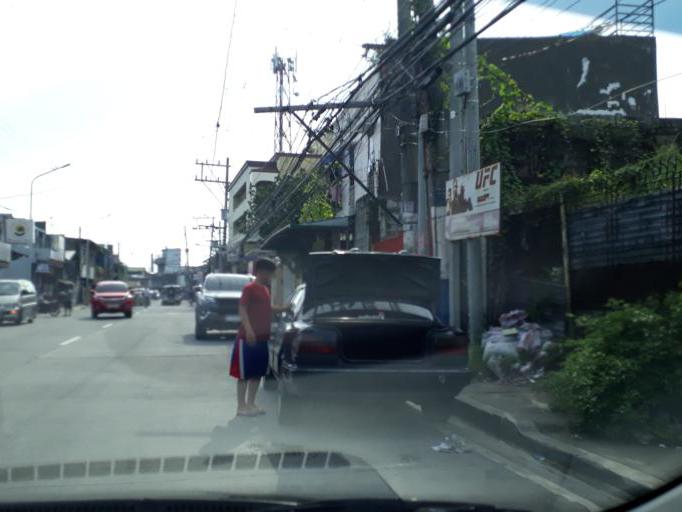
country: PH
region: Calabarzon
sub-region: Province of Rizal
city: Navotas
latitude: 14.6701
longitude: 120.9484
